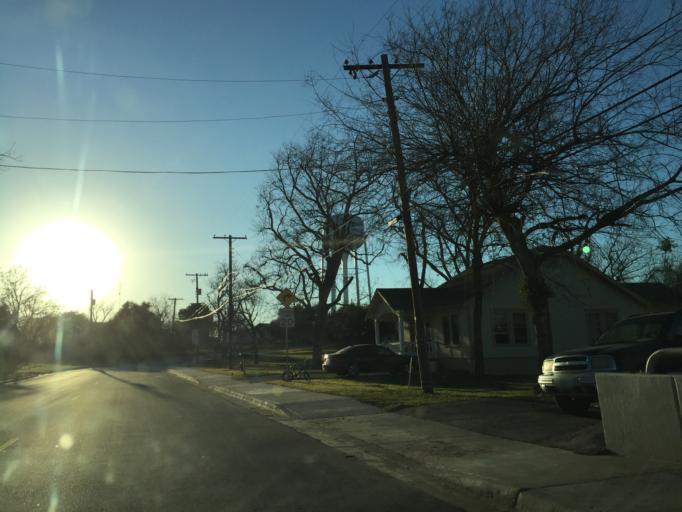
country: US
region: Texas
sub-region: Bastrop County
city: Elgin
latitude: 30.3477
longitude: -97.3759
